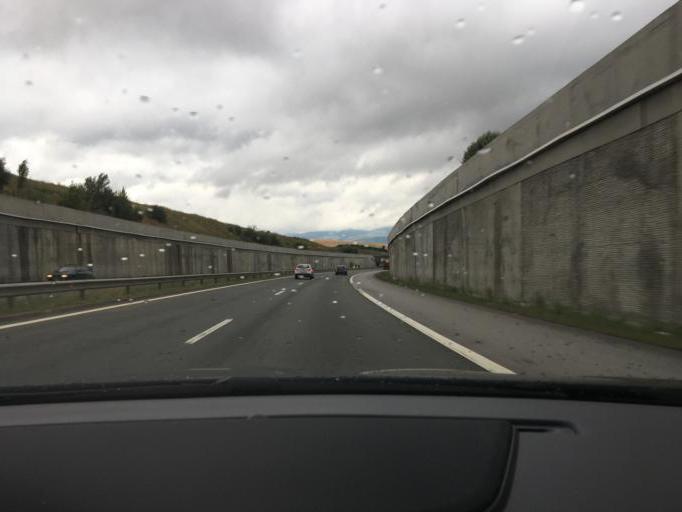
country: BG
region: Pernik
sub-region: Obshtina Pernik
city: Pernik
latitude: 42.6160
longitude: 23.1395
